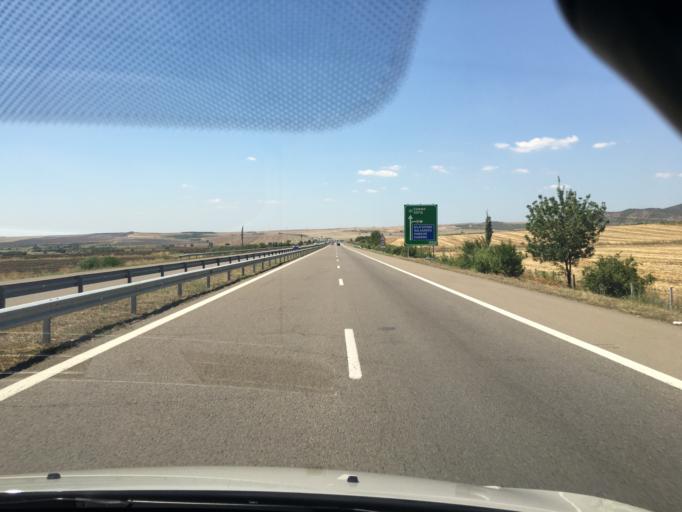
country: BG
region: Burgas
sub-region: Obshtina Kameno
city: Kameno
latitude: 42.6042
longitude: 27.3151
